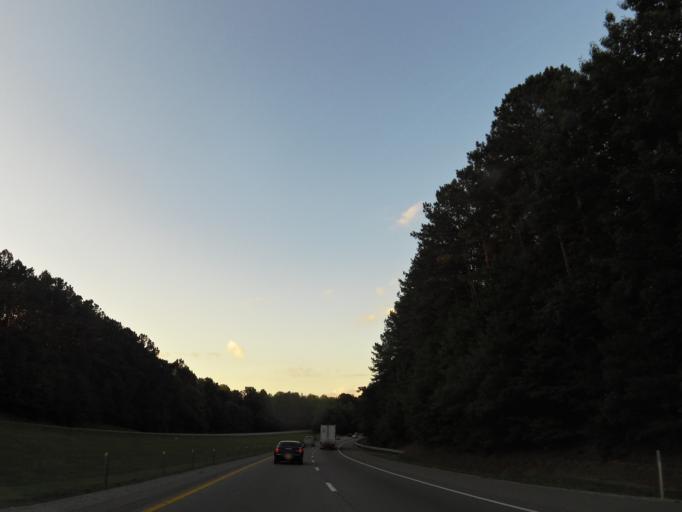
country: US
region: Tennessee
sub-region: Putnam County
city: Baxter
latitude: 36.1217
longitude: -85.6841
